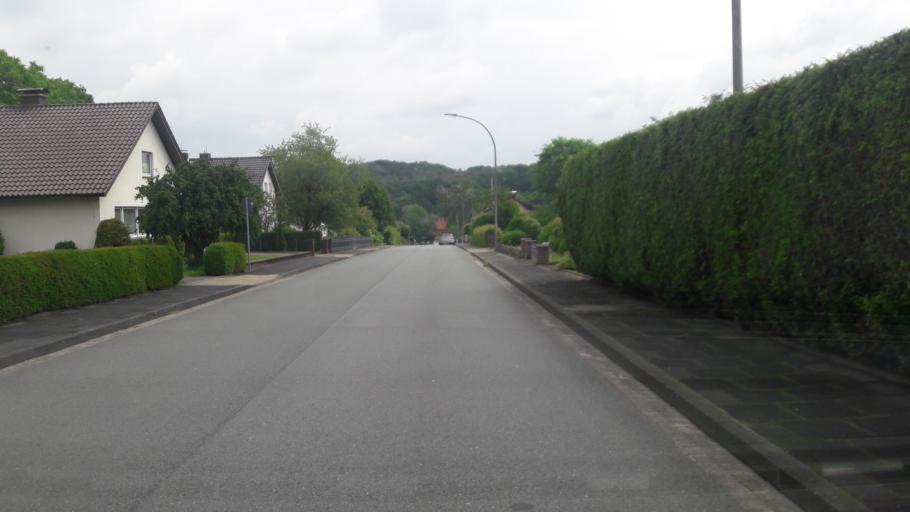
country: DE
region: North Rhine-Westphalia
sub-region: Regierungsbezirk Detmold
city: Augustdorf
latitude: 51.9430
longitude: 8.7725
